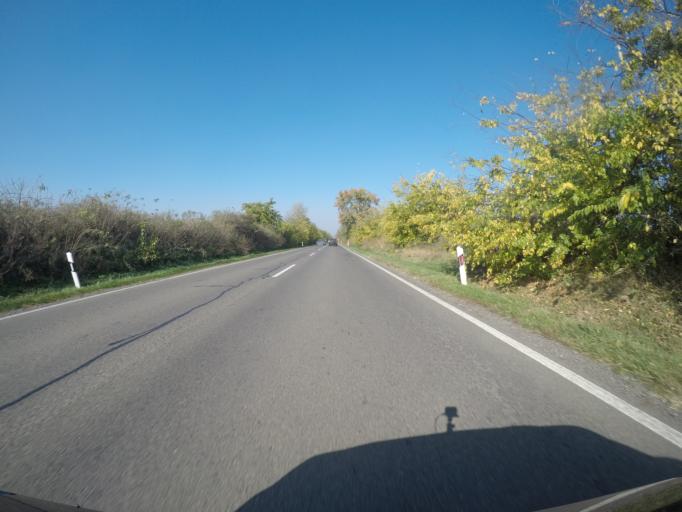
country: HU
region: Tolna
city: Tengelic
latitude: 46.5234
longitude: 18.6600
